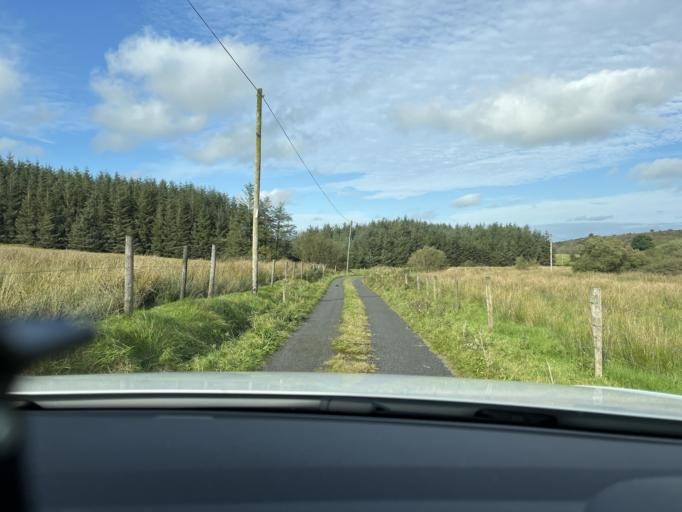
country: IE
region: Connaught
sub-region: Sligo
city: Ballymote
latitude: 54.0674
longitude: -8.4261
